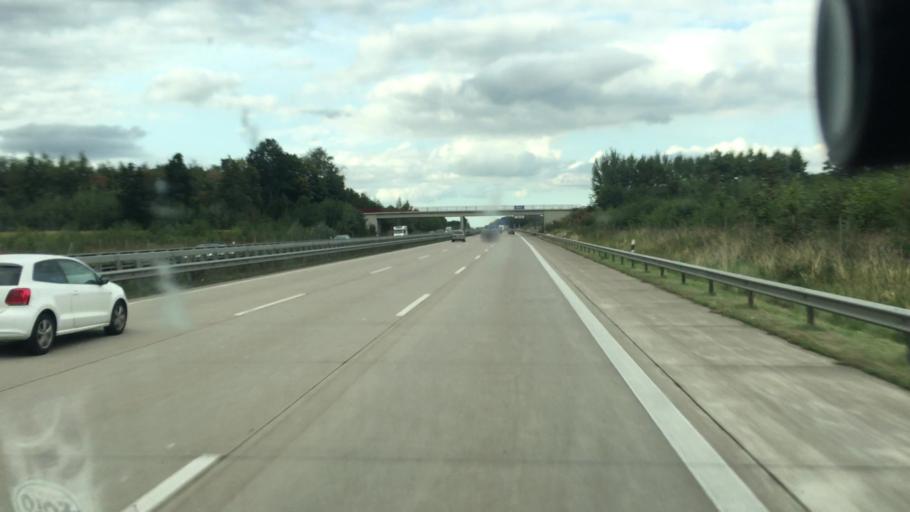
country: DE
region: Lower Saxony
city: Buehren
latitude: 52.7949
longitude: 8.2047
